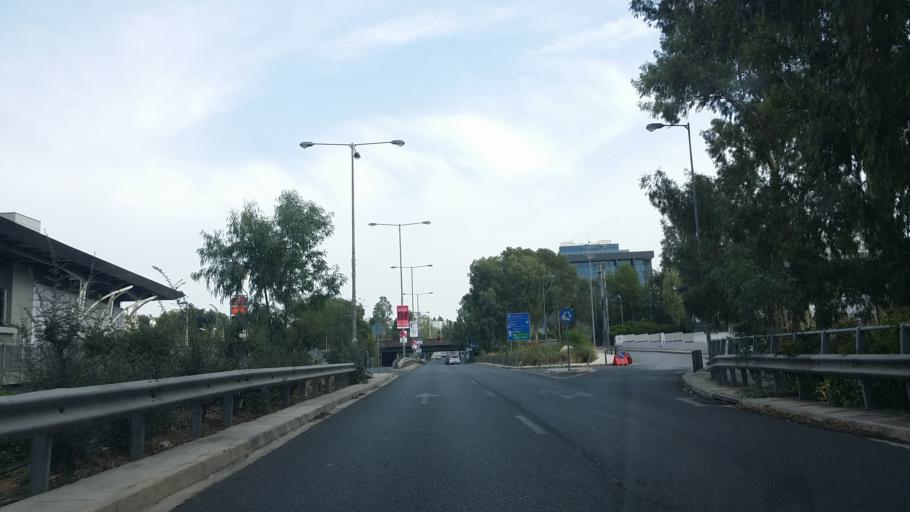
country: GR
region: Attica
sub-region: Nomarchia Athinas
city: Filothei
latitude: 38.0333
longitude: 23.7921
